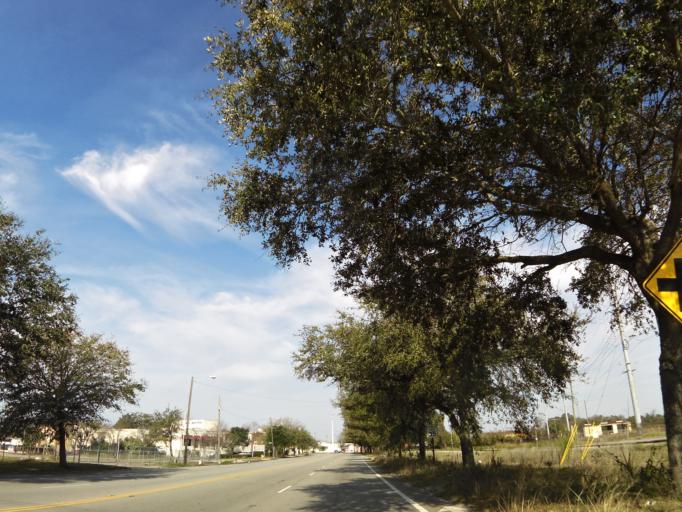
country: US
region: South Carolina
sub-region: Charleston County
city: Charleston
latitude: 32.8079
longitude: -79.9433
